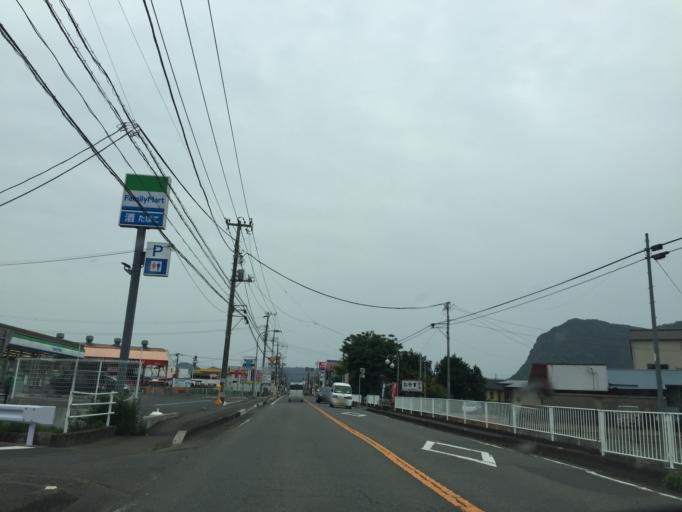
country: JP
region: Shizuoka
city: Mishima
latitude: 35.0209
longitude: 138.9458
